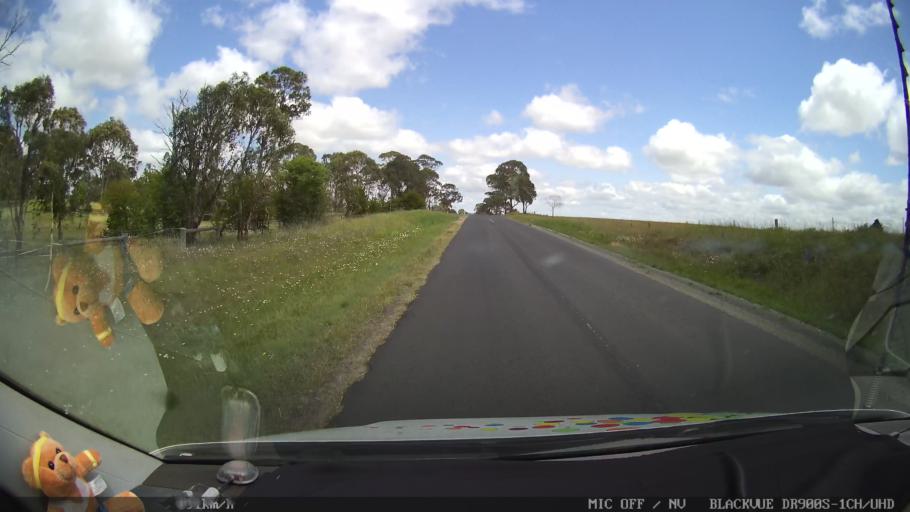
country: AU
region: New South Wales
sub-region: Glen Innes Severn
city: Glen Innes
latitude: -29.6972
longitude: 151.7166
